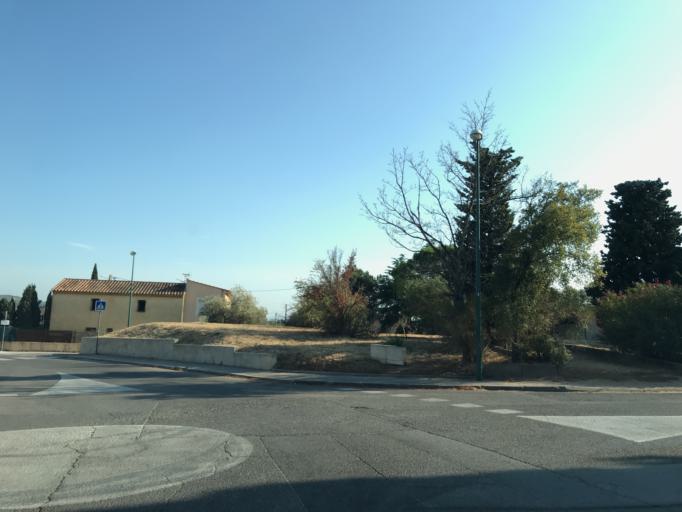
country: FR
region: Provence-Alpes-Cote d'Azur
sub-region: Departement des Bouches-du-Rhone
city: La Fare-les-Oliviers
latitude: 43.5497
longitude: 5.1887
